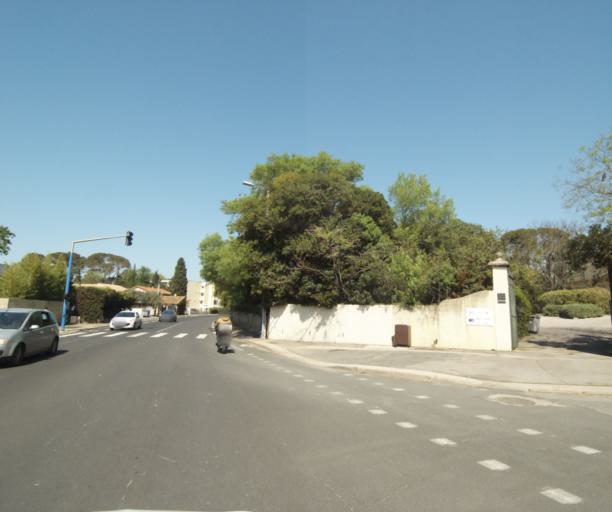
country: FR
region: Languedoc-Roussillon
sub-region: Departement de l'Herault
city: Montpellier
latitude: 43.6272
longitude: 3.8474
